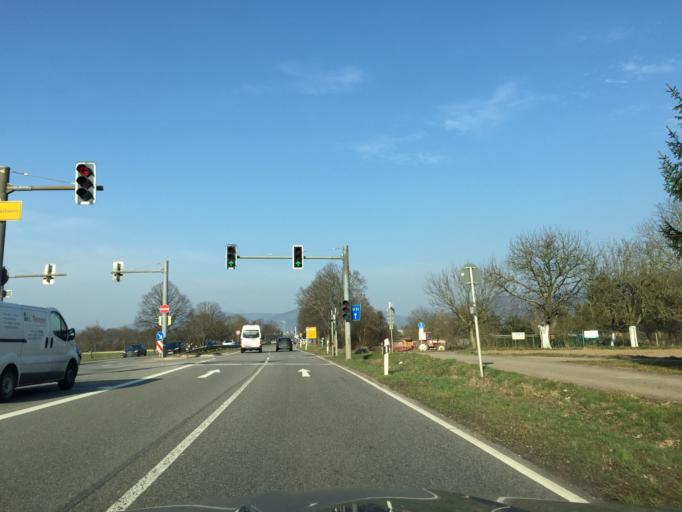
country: DE
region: Baden-Wuerttemberg
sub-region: Karlsruhe Region
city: Eppelheim
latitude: 49.3812
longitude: 8.6527
